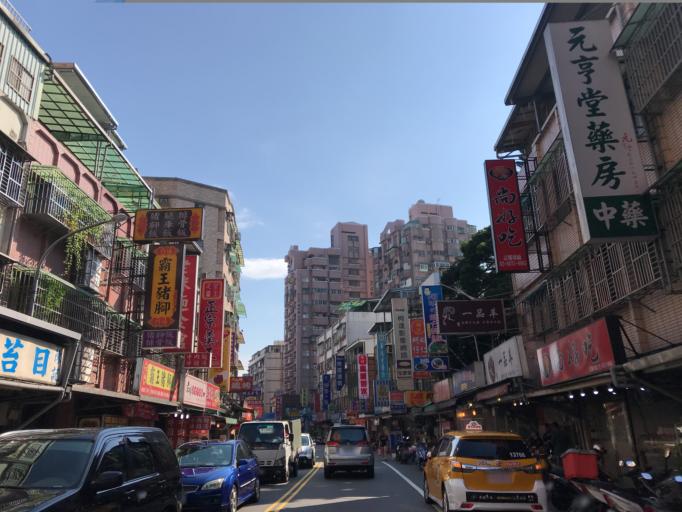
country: TW
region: Taiwan
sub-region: Taoyuan
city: Taoyuan
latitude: 24.9379
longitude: 121.3703
